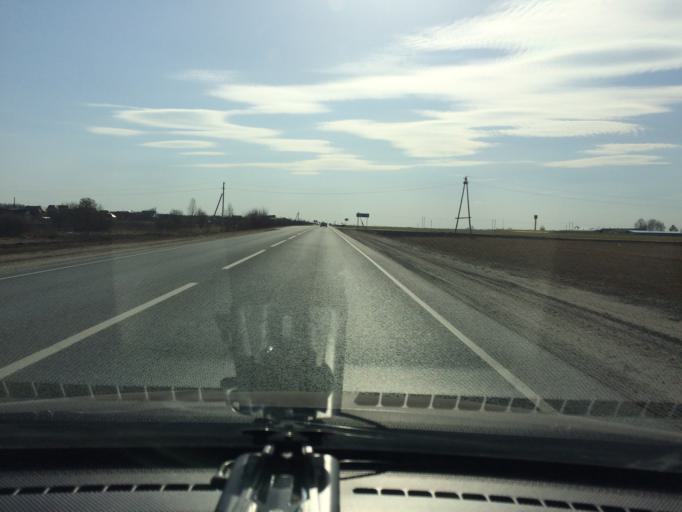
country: RU
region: Mariy-El
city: Yoshkar-Ola
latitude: 56.6713
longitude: 48.0036
